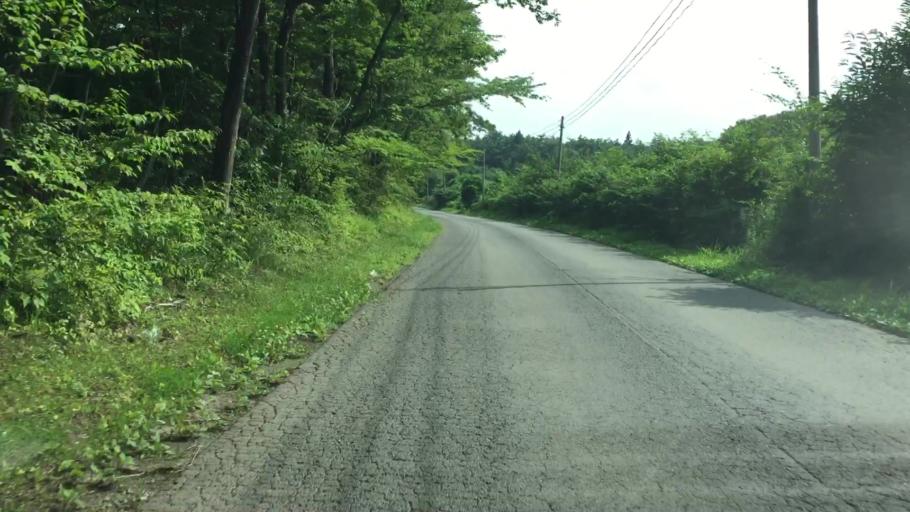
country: JP
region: Tochigi
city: Kuroiso
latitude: 37.0387
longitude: 139.9509
